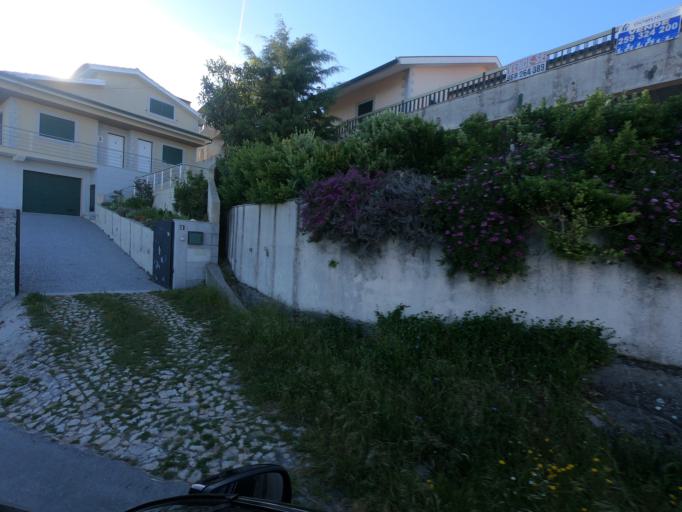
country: PT
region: Vila Real
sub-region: Vila Real
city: Vila Real
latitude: 41.3501
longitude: -7.7475
